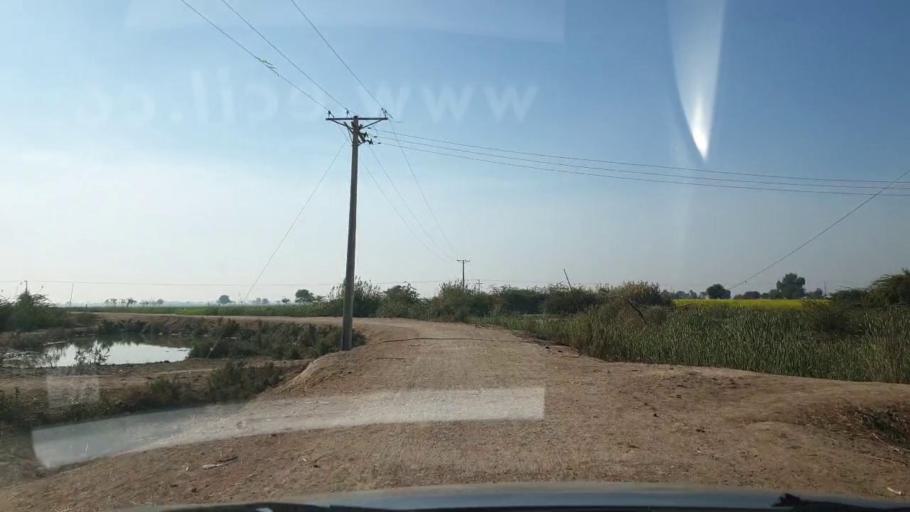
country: PK
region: Sindh
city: Berani
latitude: 25.8089
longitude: 68.9714
